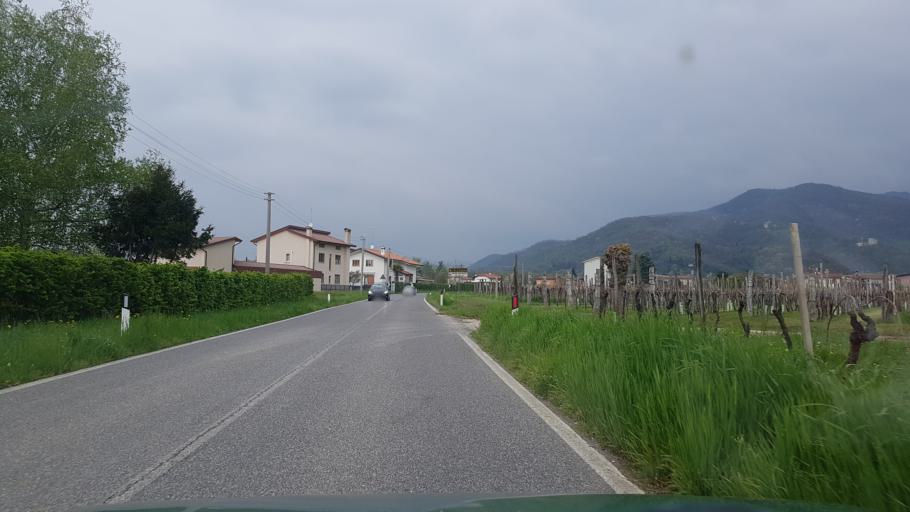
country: IT
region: Friuli Venezia Giulia
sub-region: Provincia di Udine
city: Faedis
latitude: 46.1418
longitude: 13.3481
